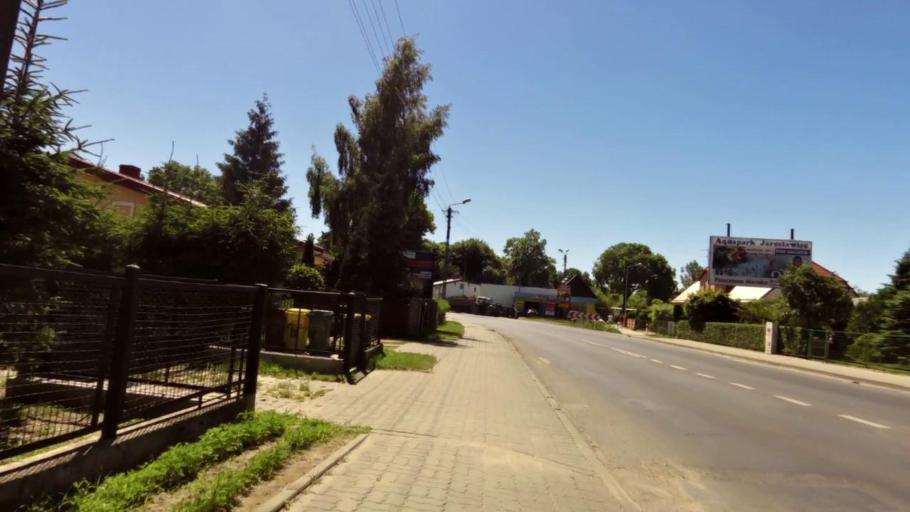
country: PL
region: West Pomeranian Voivodeship
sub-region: Powiat kolobrzeski
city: Kolobrzeg
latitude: 54.1431
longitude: 15.5591
